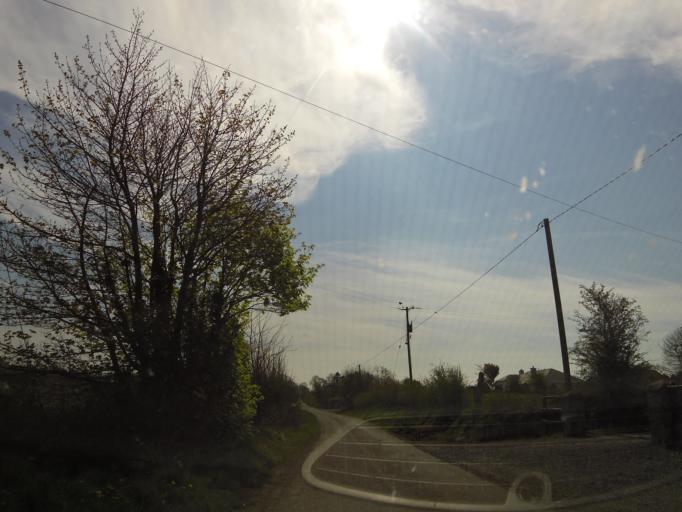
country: IE
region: Connaught
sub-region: Maigh Eo
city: Kiltamagh
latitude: 53.8000
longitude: -8.9701
